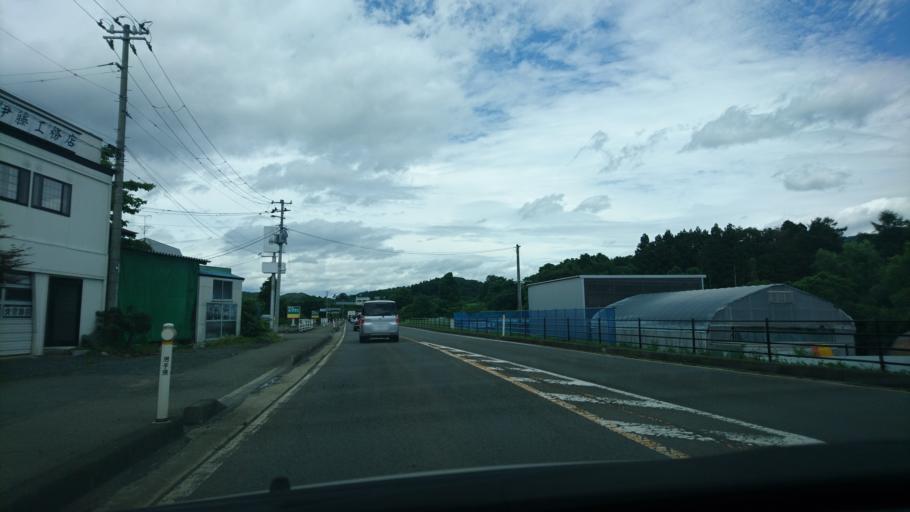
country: JP
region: Iwate
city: Morioka-shi
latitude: 39.6082
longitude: 141.2036
